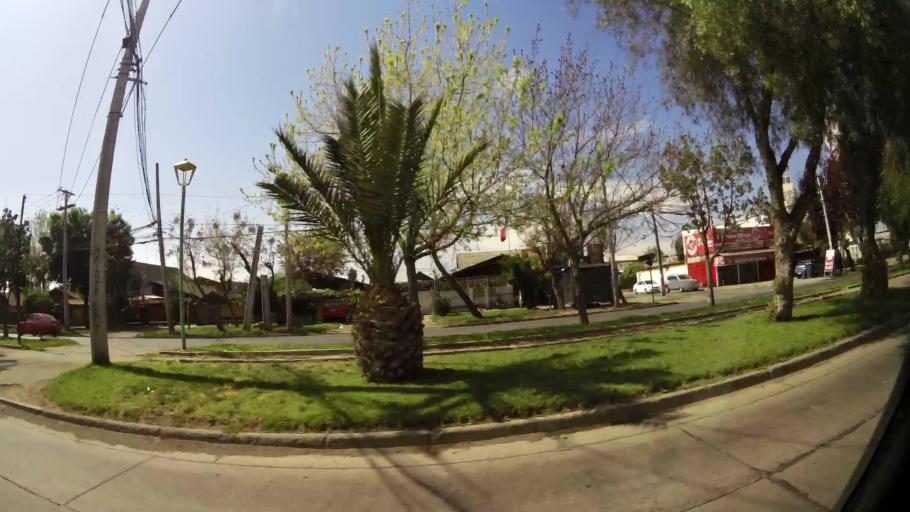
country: CL
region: Santiago Metropolitan
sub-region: Provincia de Santiago
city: Lo Prado
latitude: -33.4781
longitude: -70.7232
